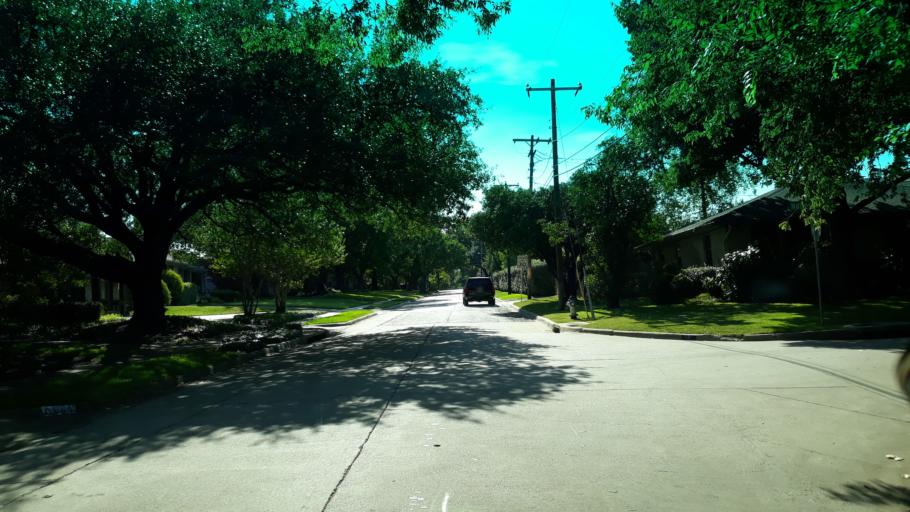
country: US
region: Texas
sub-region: Dallas County
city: Highland Park
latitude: 32.8220
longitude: -96.7480
